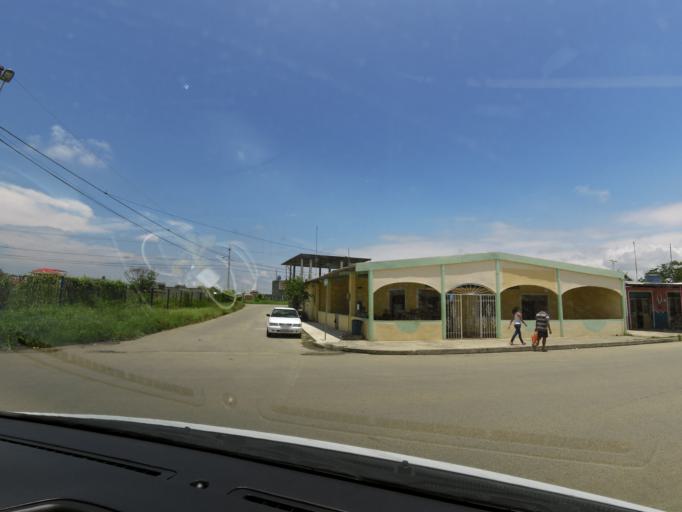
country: EC
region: El Oro
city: Huaquillas
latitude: -3.4708
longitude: -80.2334
